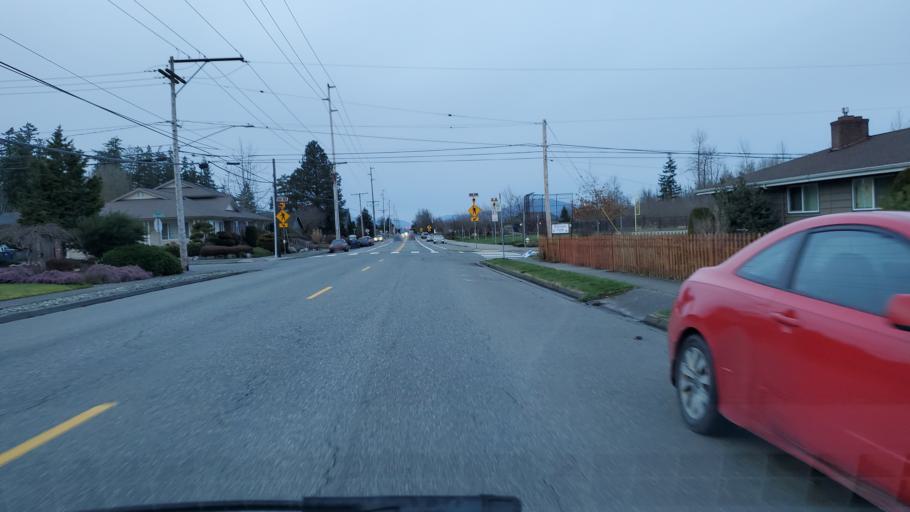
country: US
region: Washington
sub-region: Skagit County
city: Mount Vernon
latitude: 48.4161
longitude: -122.3188
